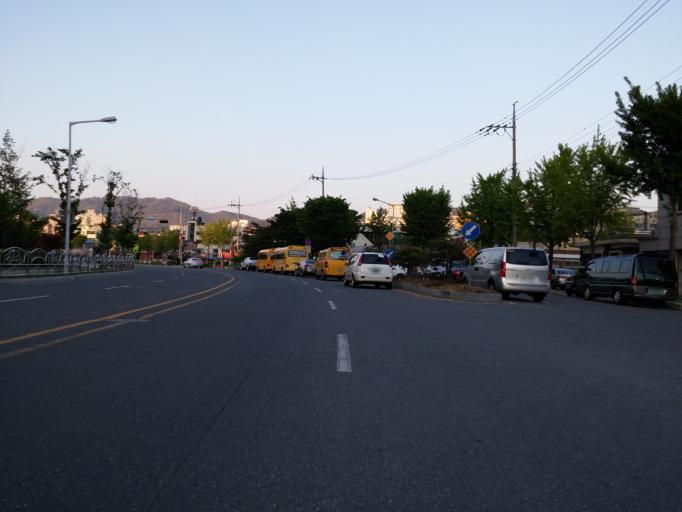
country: KR
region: Daejeon
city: Daejeon
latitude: 36.3402
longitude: 127.4413
